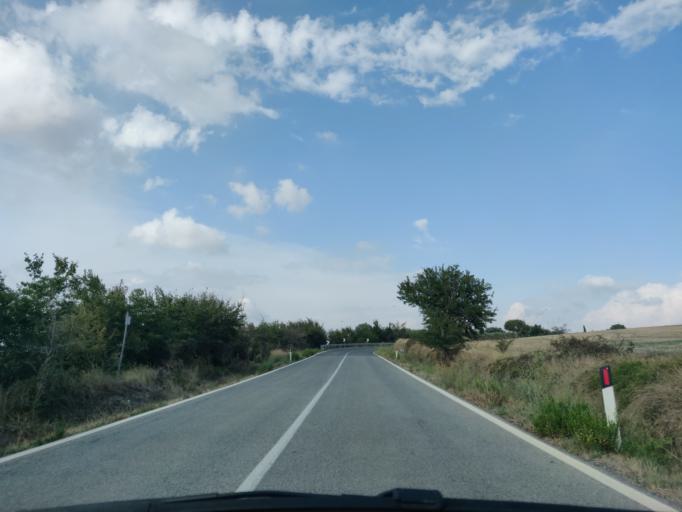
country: IT
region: Latium
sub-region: Provincia di Viterbo
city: Tarquinia
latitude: 42.2216
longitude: 11.7858
